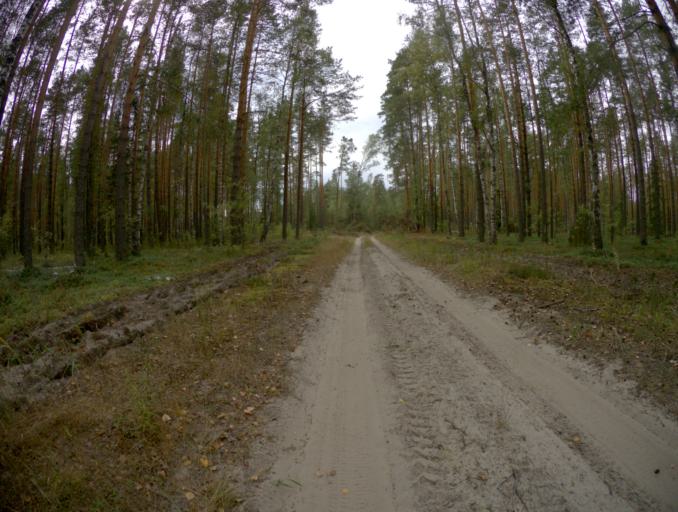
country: RU
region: Vladimir
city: Ivanishchi
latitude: 55.8557
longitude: 40.3682
